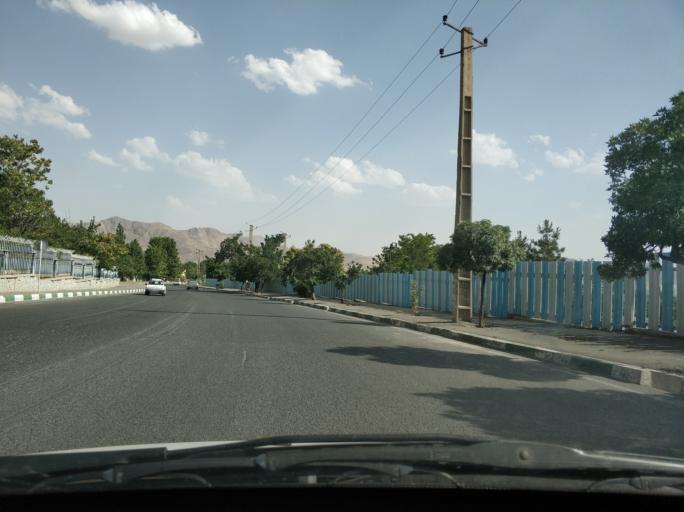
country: IR
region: Tehran
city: Tajrish
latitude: 35.7485
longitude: 51.5763
